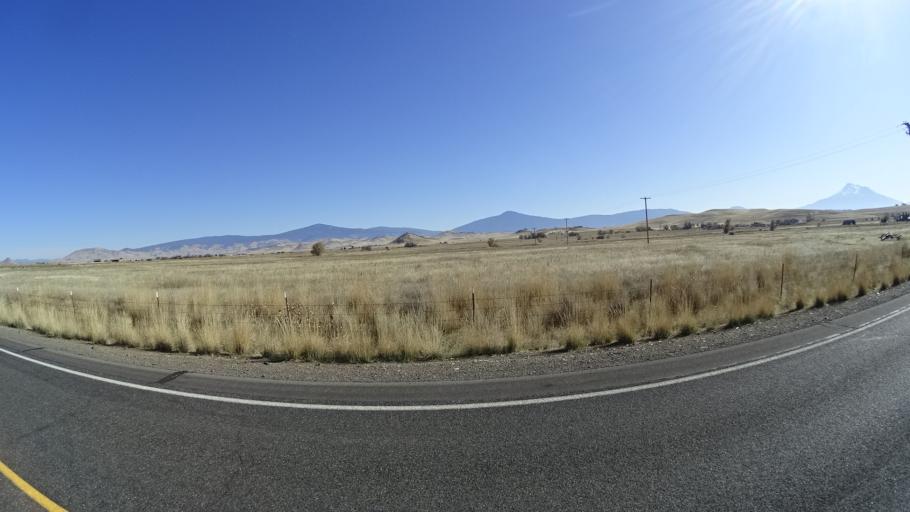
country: US
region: California
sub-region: Siskiyou County
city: Montague
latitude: 41.7478
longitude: -122.5247
